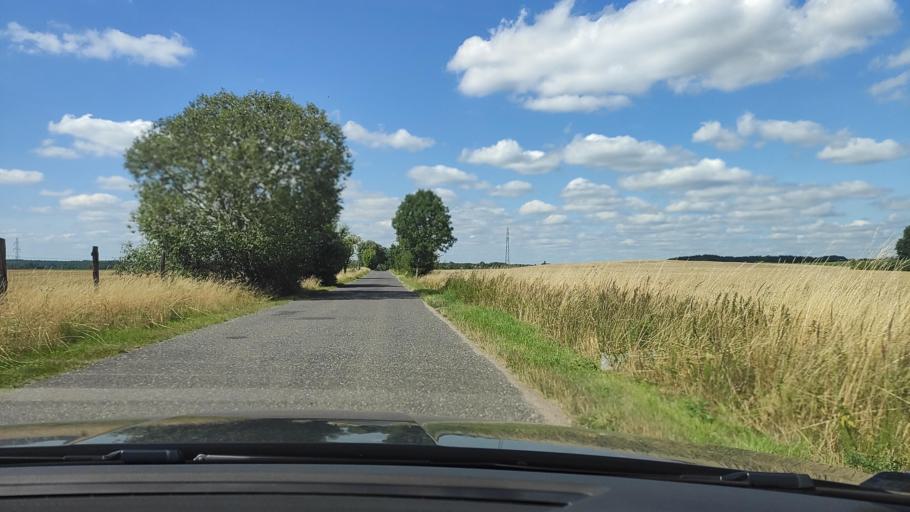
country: PL
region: Greater Poland Voivodeship
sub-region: Powiat poznanski
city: Kobylnica
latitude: 52.4865
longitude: 17.1353
